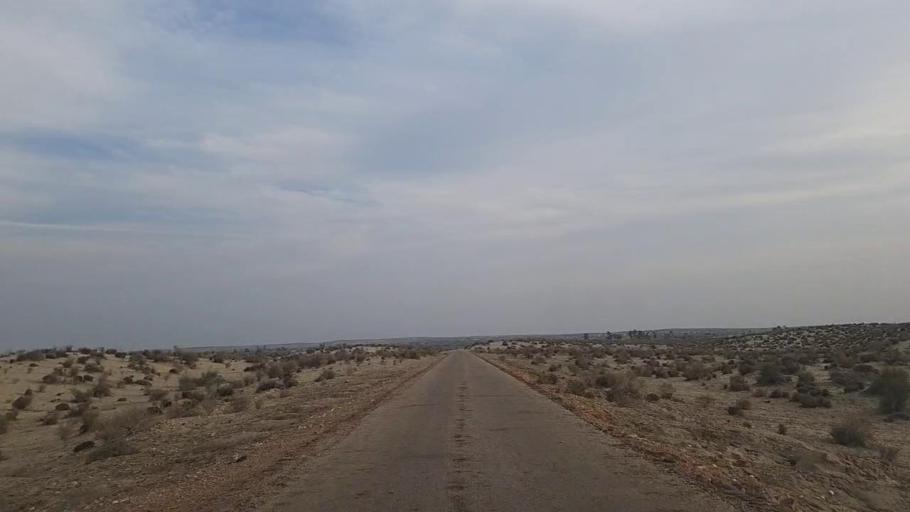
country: PK
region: Sindh
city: Daur
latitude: 26.5021
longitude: 68.5198
